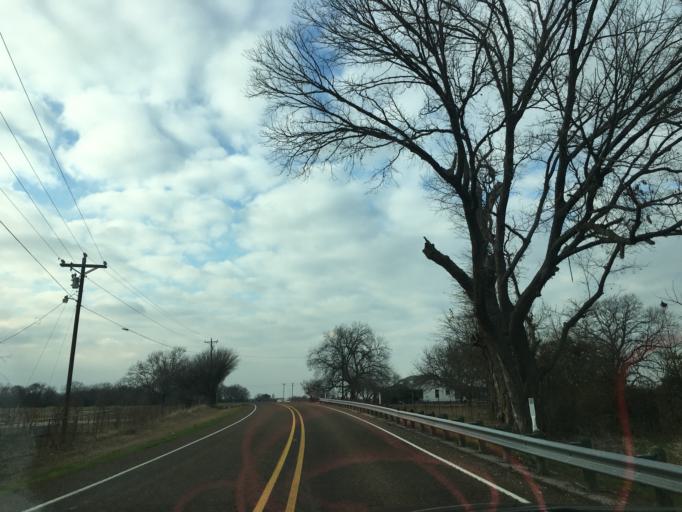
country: US
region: Texas
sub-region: Ellis County
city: Palmer
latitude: 32.4528
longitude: -96.7353
